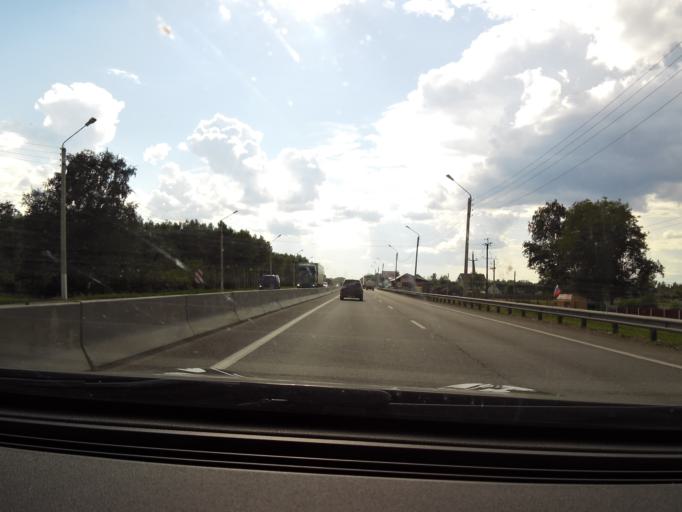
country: RU
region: Nizjnij Novgorod
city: Babino
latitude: 56.3041
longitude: 43.6149
